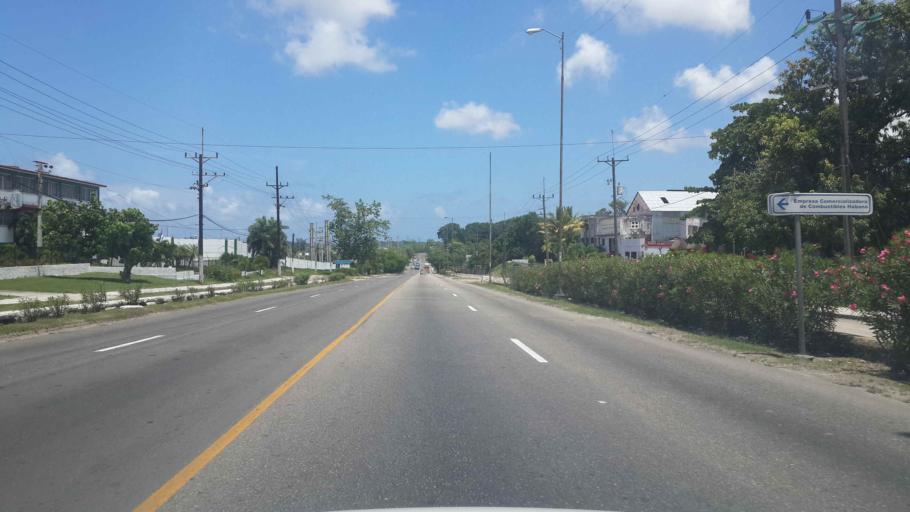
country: CU
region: La Habana
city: Regla
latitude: 23.1281
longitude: -82.3161
